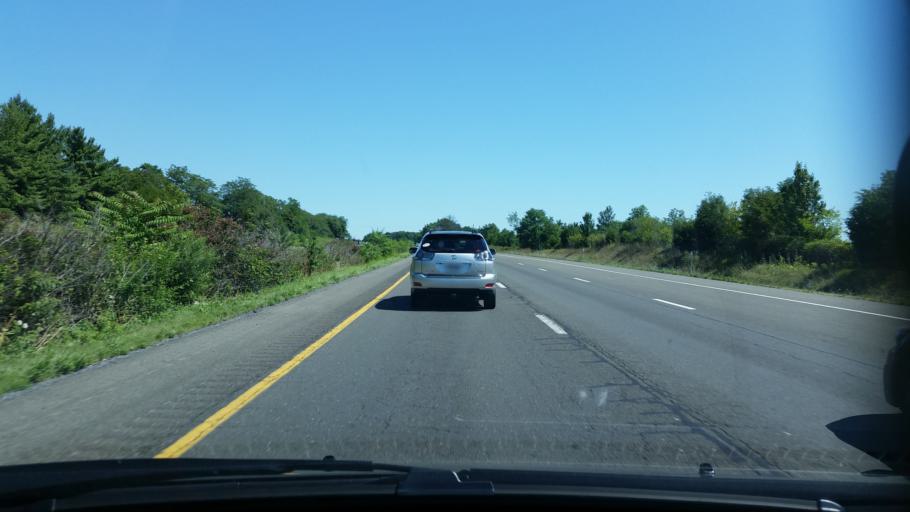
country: US
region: Virginia
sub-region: Frederick County
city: Stephens City
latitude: 39.0862
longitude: -78.2110
